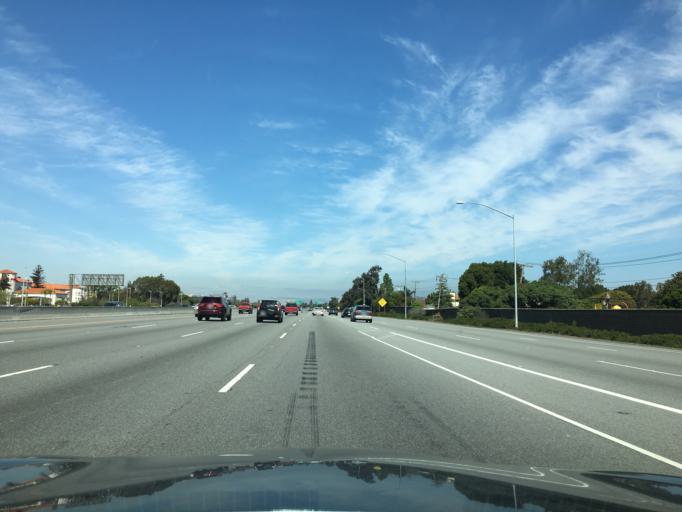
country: US
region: California
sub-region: San Mateo County
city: Foster City
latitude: 37.5553
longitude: -122.2977
